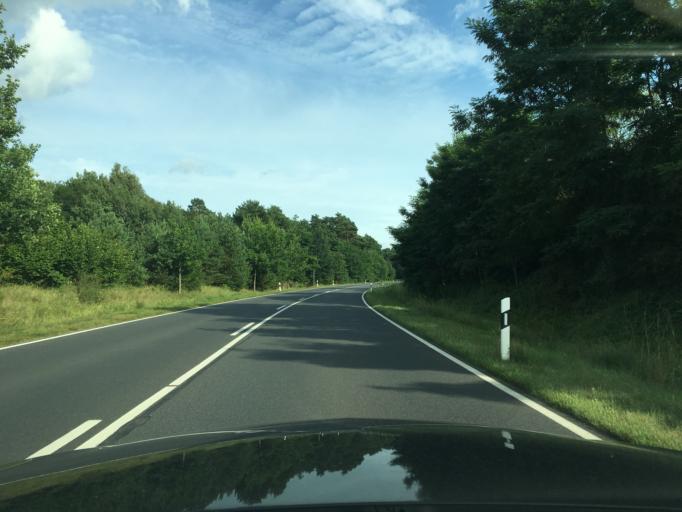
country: DE
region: Mecklenburg-Vorpommern
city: Neustrelitz
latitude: 53.3771
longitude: 13.0687
